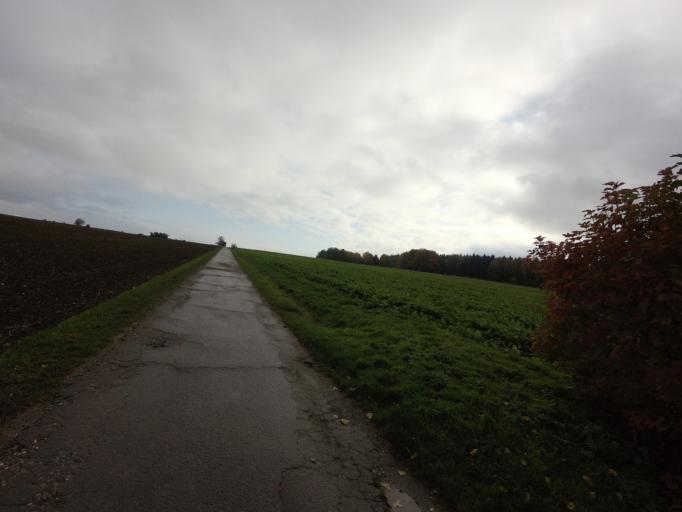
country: NL
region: Limburg
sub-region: Gemeente Vaals
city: Vaals
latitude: 50.7896
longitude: 6.0173
